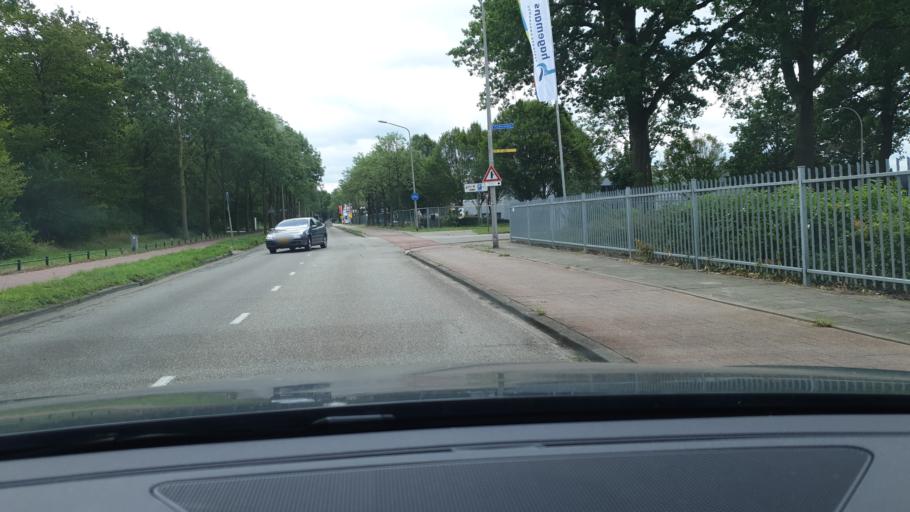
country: NL
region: Gelderland
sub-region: Gemeente Nijmegen
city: Lindenholt
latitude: 51.8188
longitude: 5.8231
